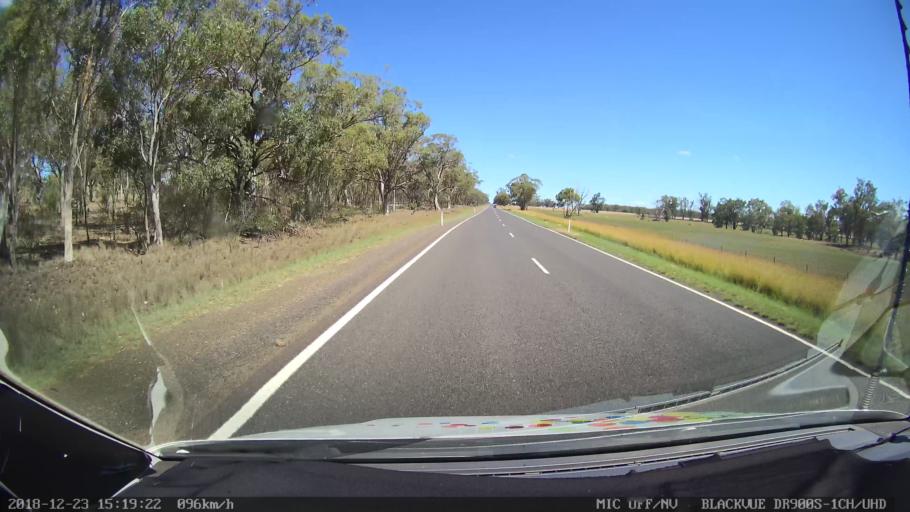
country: AU
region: New South Wales
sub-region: Tamworth Municipality
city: Manilla
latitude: -30.8280
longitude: 150.7823
